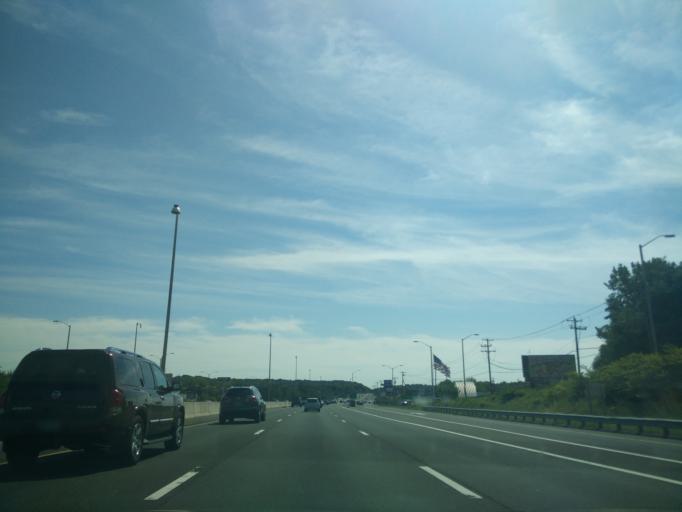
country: US
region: Connecticut
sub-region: New Haven County
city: East Haven
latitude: 41.2885
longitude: -72.8886
